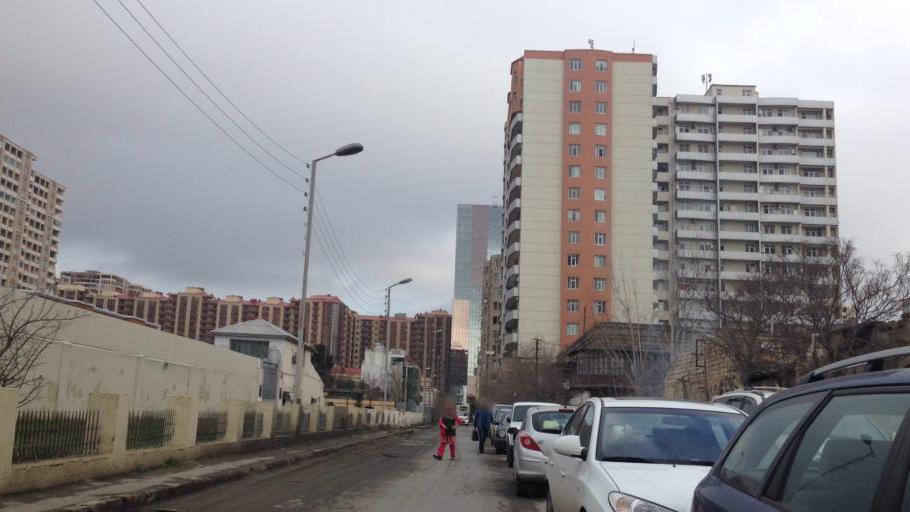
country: AZ
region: Baki
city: Baku
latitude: 40.3790
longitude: 49.8722
